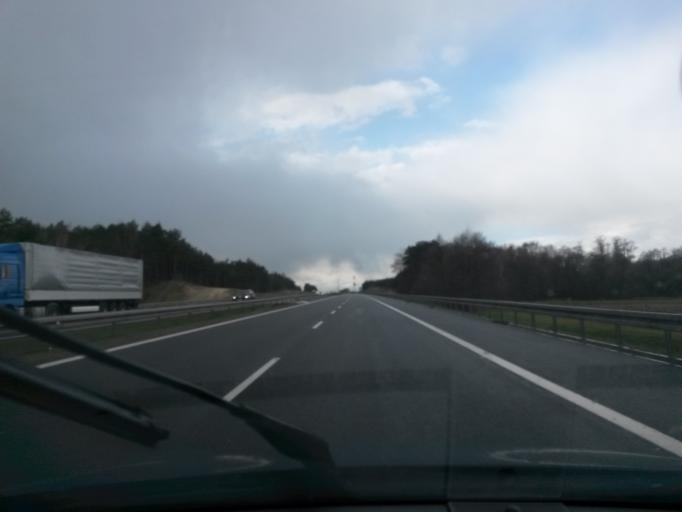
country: PL
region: Greater Poland Voivodeship
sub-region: Powiat koninski
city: Golina
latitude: 52.1771
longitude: 18.1357
